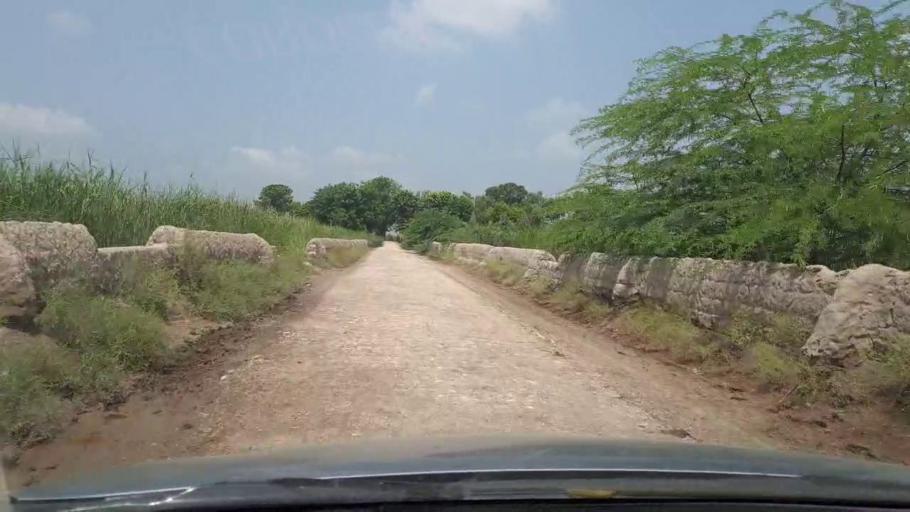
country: PK
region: Sindh
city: Khairpur
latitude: 27.4804
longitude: 68.7108
